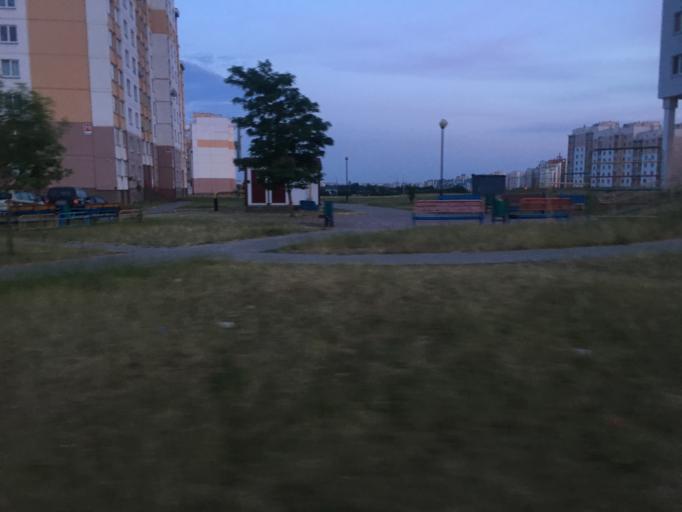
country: BY
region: Grodnenskaya
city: Hrodna
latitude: 53.7138
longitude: 23.8642
